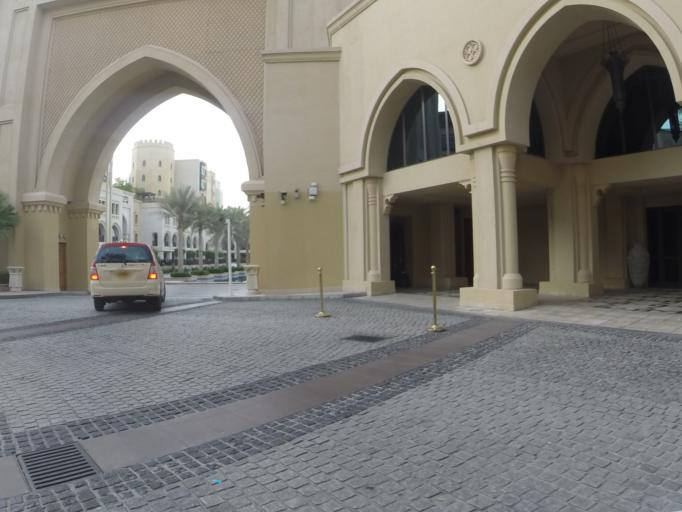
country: AE
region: Dubai
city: Dubai
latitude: 25.1926
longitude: 55.2770
